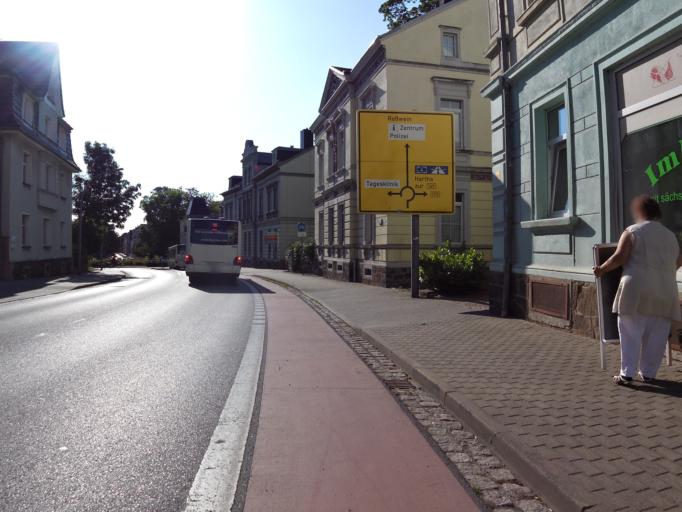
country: DE
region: Saxony
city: Dobeln
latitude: 51.1226
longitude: 13.1038
